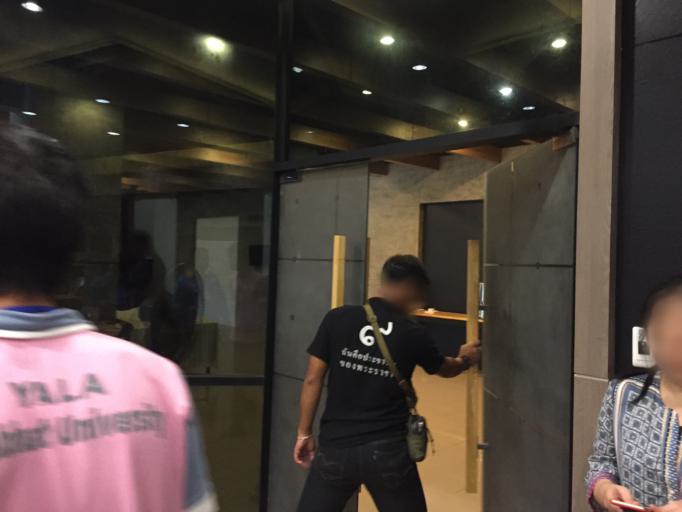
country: TH
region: Pattani
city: Pattani
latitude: 6.8553
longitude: 101.2171
